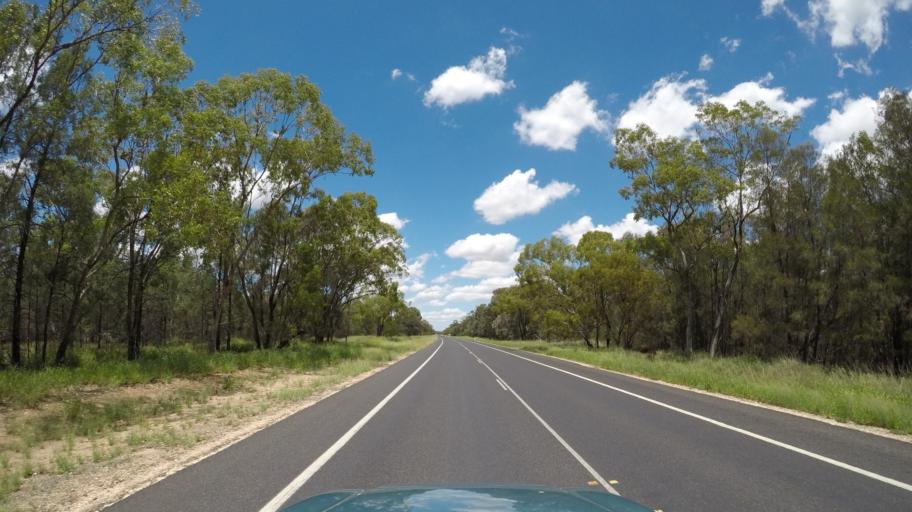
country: AU
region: Queensland
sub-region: Goondiwindi
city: Goondiwindi
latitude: -28.0934
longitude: 150.7281
